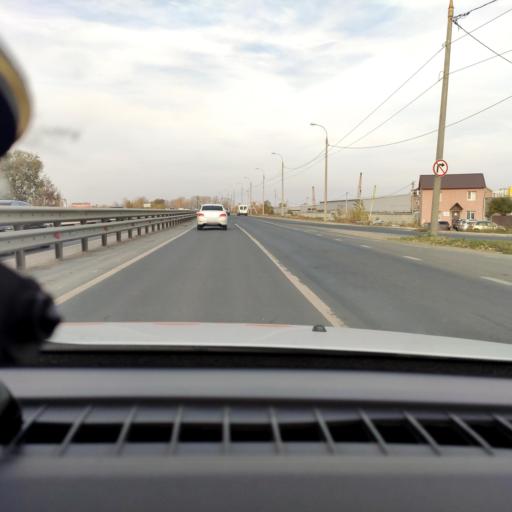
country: RU
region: Samara
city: Samara
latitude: 53.0971
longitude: 50.1582
